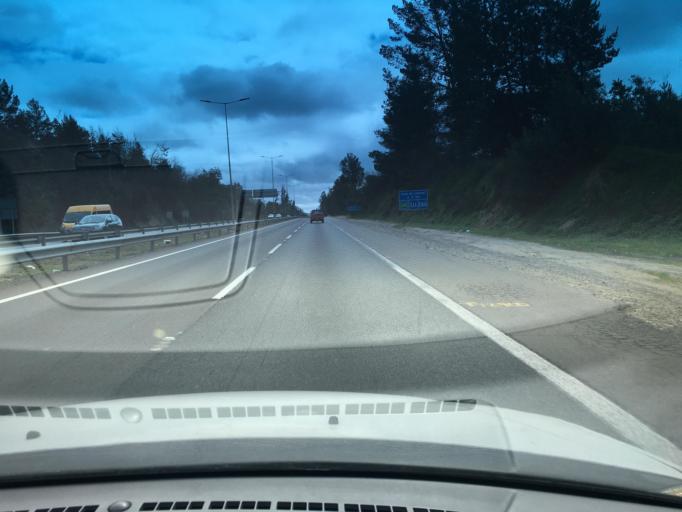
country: CL
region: Valparaiso
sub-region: Provincia de Valparaiso
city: Vina del Mar
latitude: -33.1607
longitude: -71.5429
